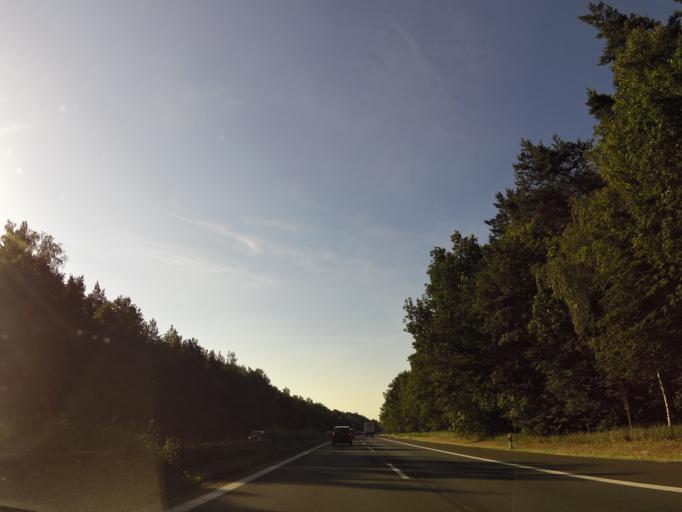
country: DE
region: Bavaria
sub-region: Regierungsbezirk Mittelfranken
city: Grossenseebach
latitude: 49.6643
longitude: 10.8868
